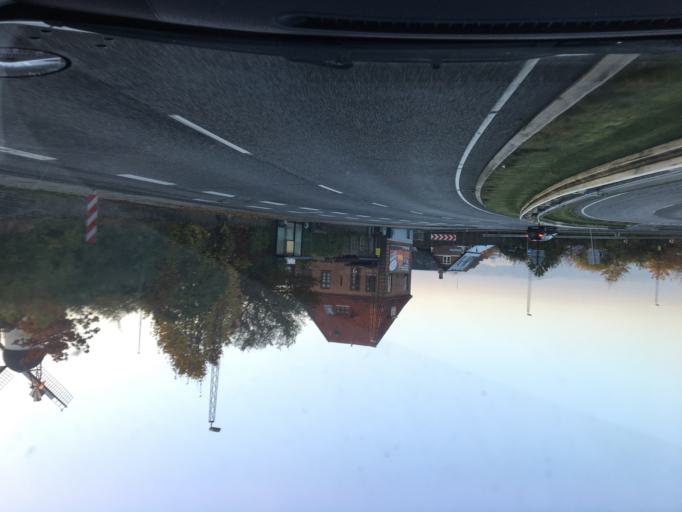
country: DK
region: South Denmark
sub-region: Vejle Kommune
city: Vejle
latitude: 55.6993
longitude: 9.5294
